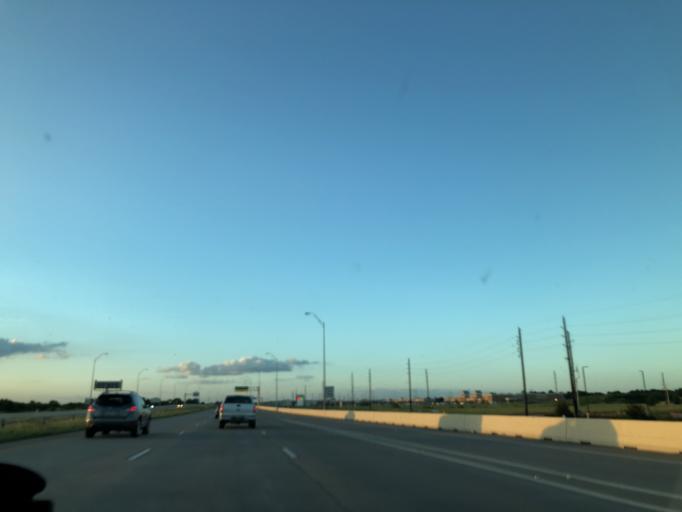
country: US
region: Texas
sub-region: Harris County
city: Katy
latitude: 29.8073
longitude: -95.7744
